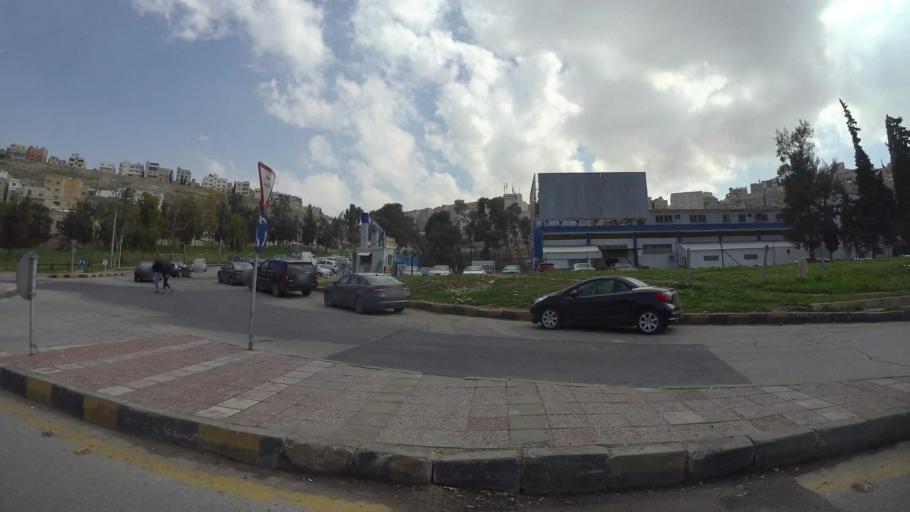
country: JO
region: Amman
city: Amman
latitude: 31.9812
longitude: 35.9763
